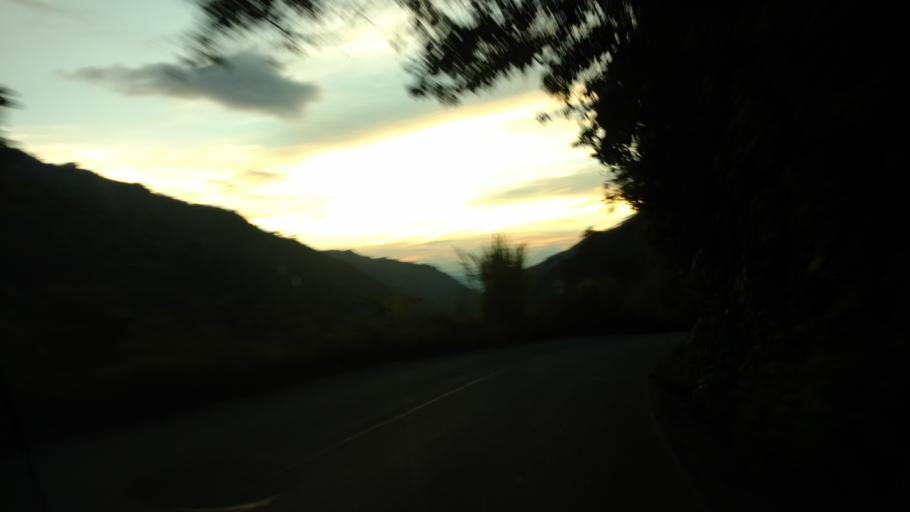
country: CO
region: Caldas
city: Aranzazu
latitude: 5.2555
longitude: -75.4998
